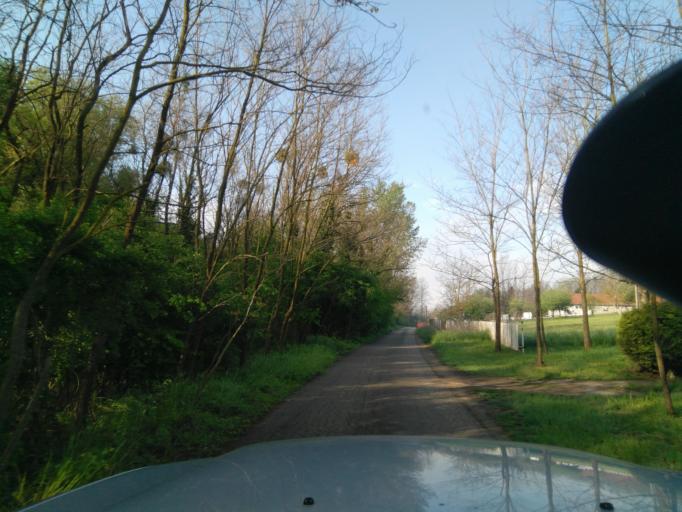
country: HU
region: Zala
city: Sarmellek
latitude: 46.7432
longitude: 17.1440
